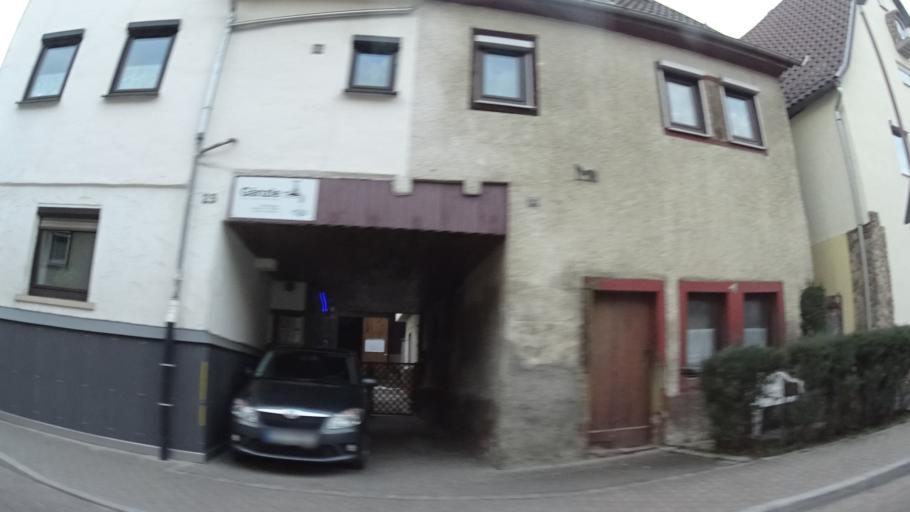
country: DE
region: Baden-Wuerttemberg
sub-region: Regierungsbezirk Stuttgart
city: Hemmingen
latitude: 48.8872
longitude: 9.0032
